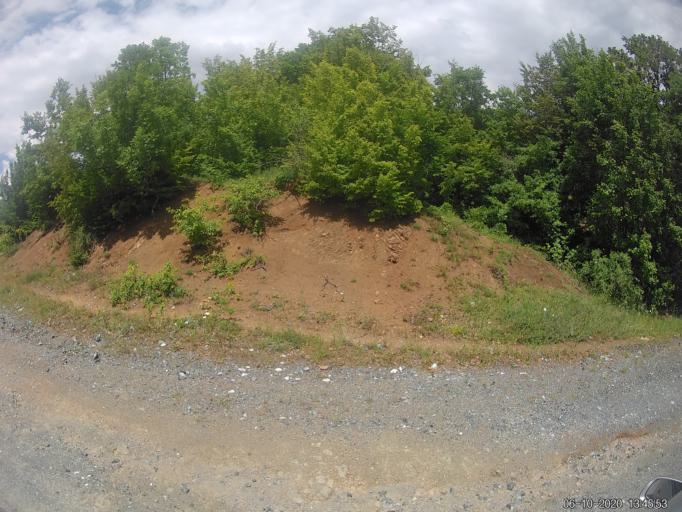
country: XK
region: Prizren
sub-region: Komuna e Therandes
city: Budakovo
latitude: 42.4097
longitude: 20.9151
